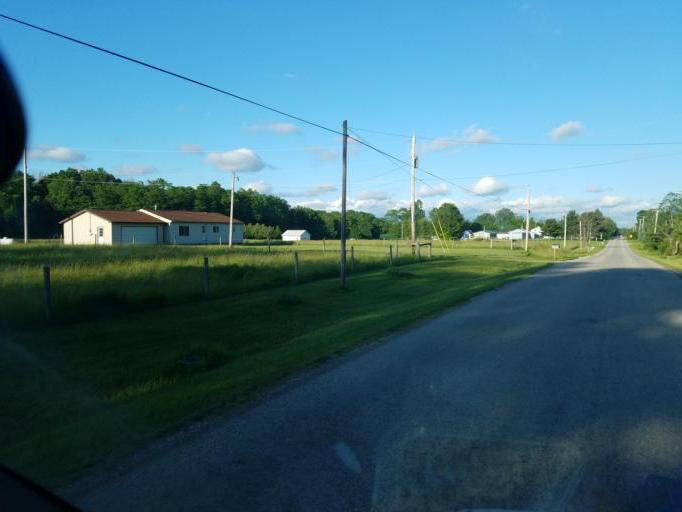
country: US
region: Ohio
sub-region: Morrow County
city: Mount Gilead
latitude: 40.4580
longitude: -82.7120
